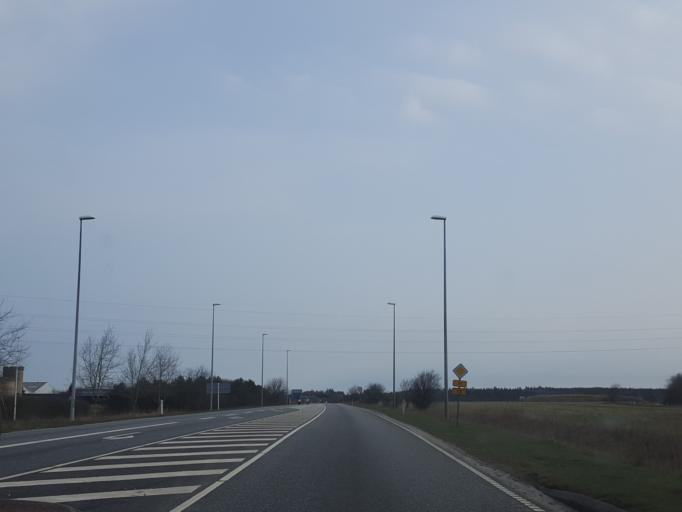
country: DK
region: South Denmark
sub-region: Varde Kommune
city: Varde
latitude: 55.6066
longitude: 8.5078
